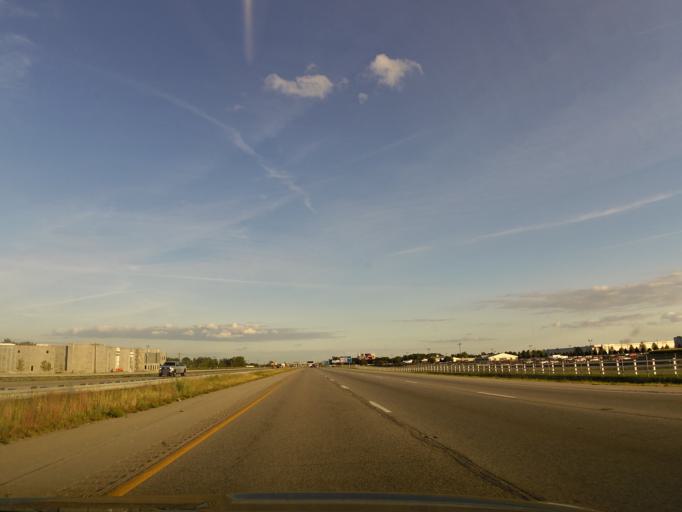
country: US
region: Indiana
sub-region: Boone County
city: Whitestown
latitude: 39.9709
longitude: -86.3830
